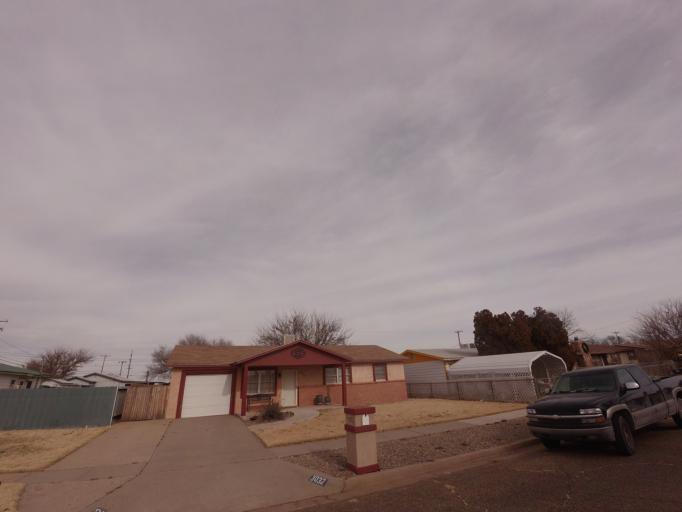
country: US
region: New Mexico
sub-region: Curry County
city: Clovis
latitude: 34.4107
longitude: -103.2443
